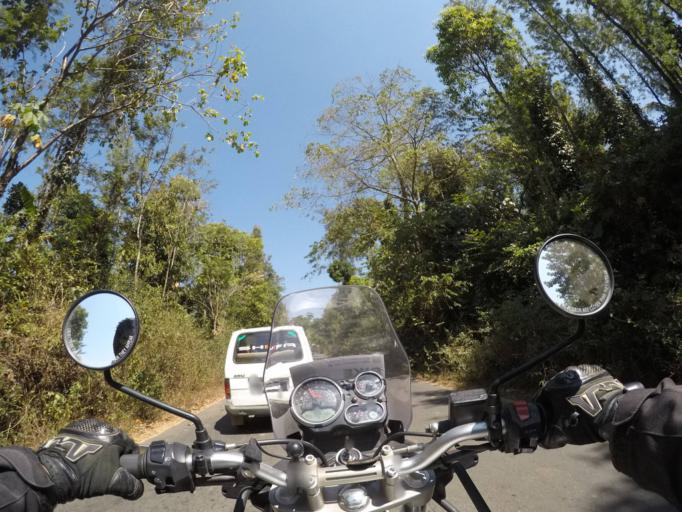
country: IN
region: Karnataka
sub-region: Chikmagalur
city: Mudigere
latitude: 13.0719
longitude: 75.6811
